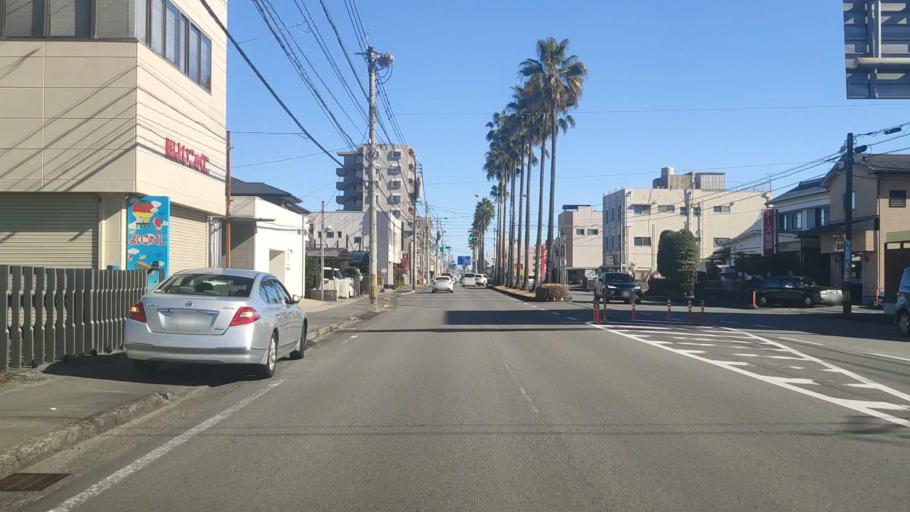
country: JP
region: Miyazaki
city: Miyazaki-shi
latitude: 31.9077
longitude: 131.4375
